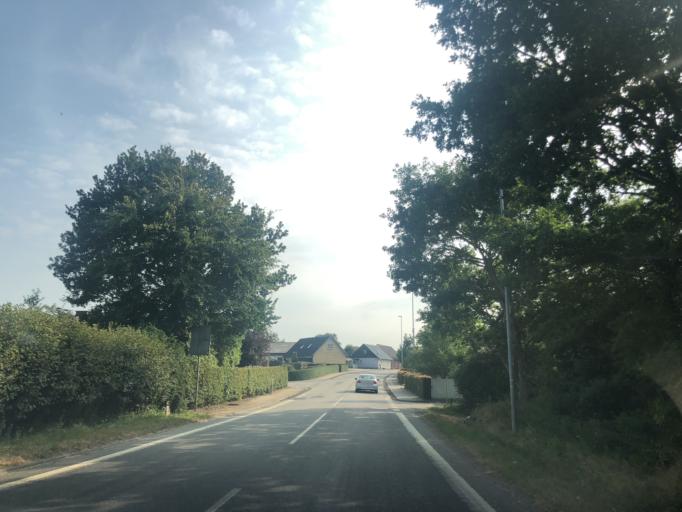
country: DK
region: Central Jutland
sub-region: Skive Kommune
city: Skive
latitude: 56.6559
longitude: 8.9367
